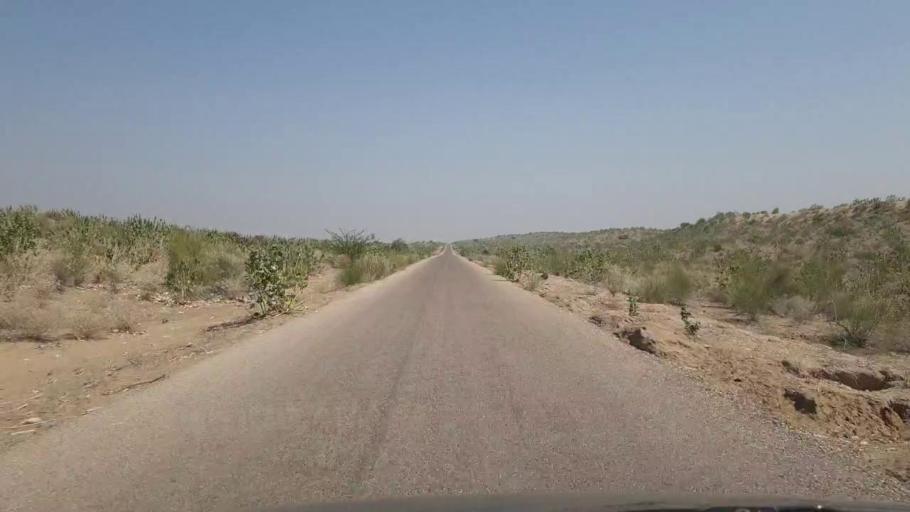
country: PK
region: Sindh
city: Chor
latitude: 25.6779
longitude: 70.1745
